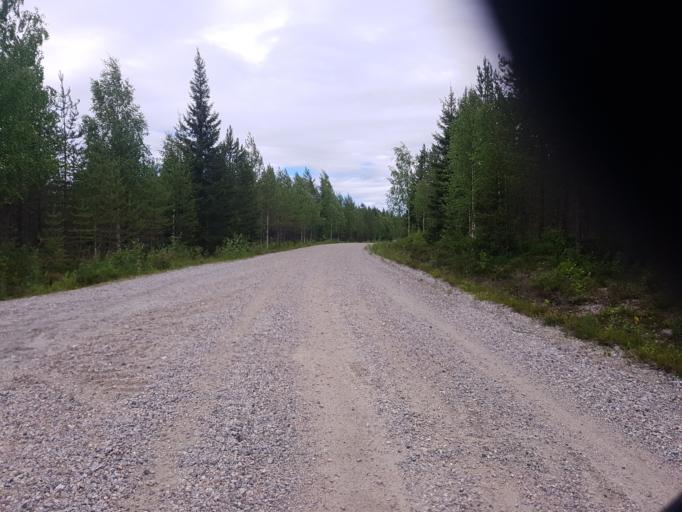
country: FI
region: Kainuu
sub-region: Kehys-Kainuu
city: Kuhmo
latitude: 64.4331
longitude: 29.5772
